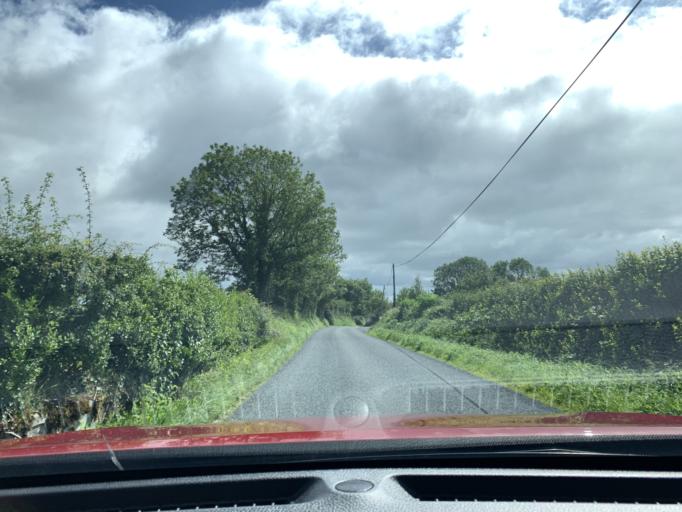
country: IE
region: Connaught
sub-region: County Leitrim
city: Carrick-on-Shannon
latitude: 53.8513
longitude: -8.1518
